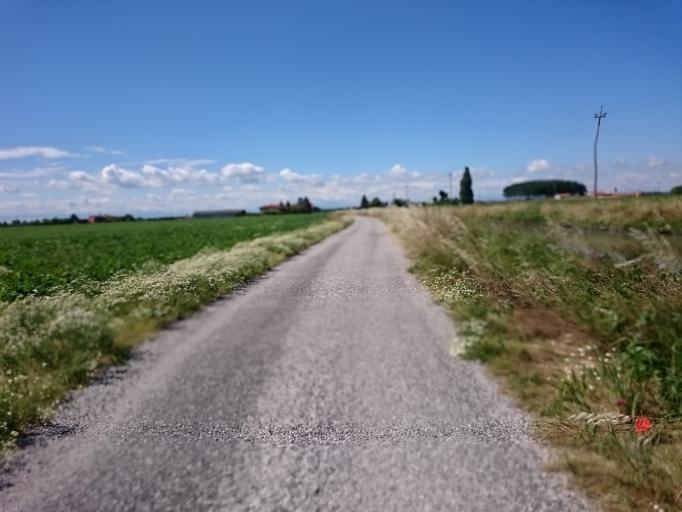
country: IT
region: Veneto
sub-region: Provincia di Padova
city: Codevigo
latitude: 45.2571
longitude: 12.0974
